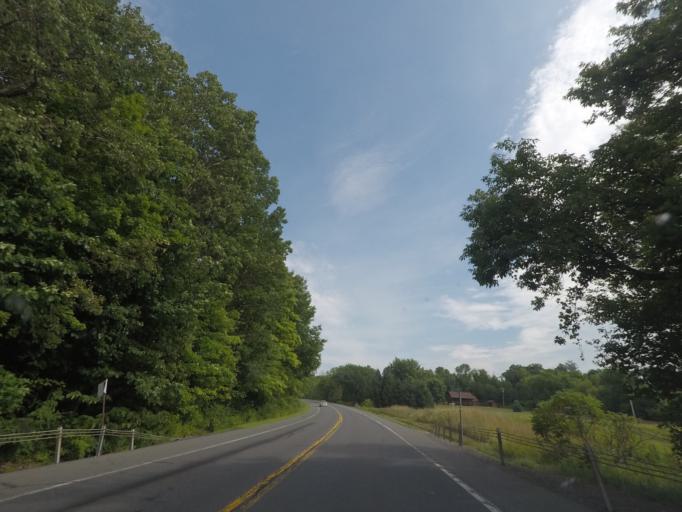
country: US
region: New York
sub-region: Rensselaer County
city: Poestenkill
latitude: 42.6965
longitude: -73.5599
